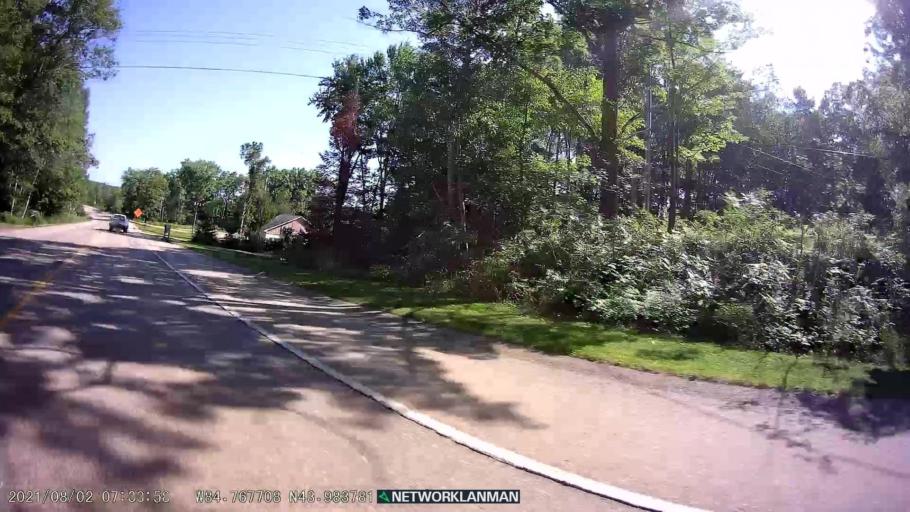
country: US
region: Michigan
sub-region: Clare County
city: Harrison
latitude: 43.9840
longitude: -84.7677
